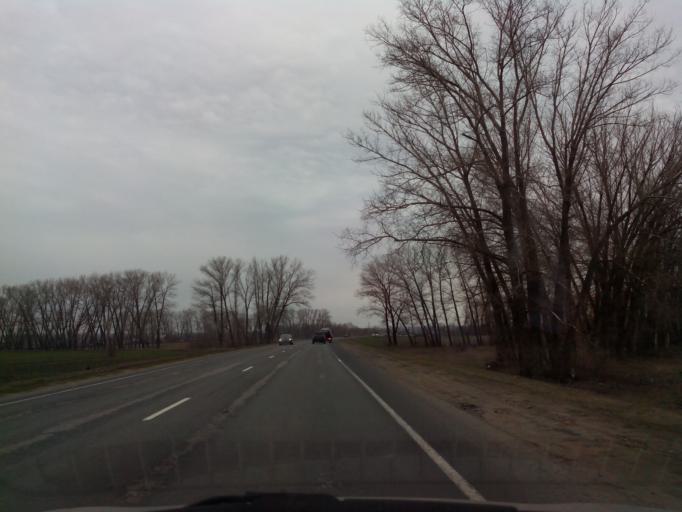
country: RU
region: Tambov
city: Zavoronezhskoye
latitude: 52.9497
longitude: 40.5851
